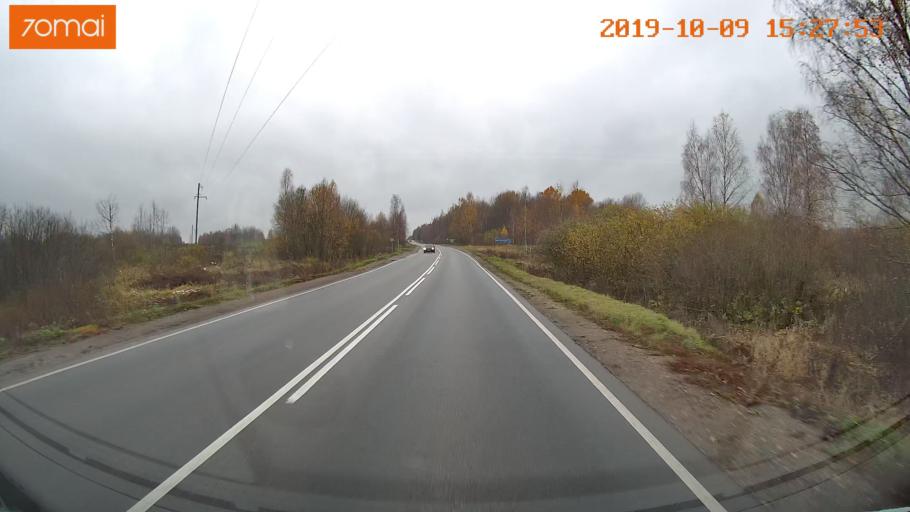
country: RU
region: Kostroma
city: Susanino
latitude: 58.0094
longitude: 41.3695
